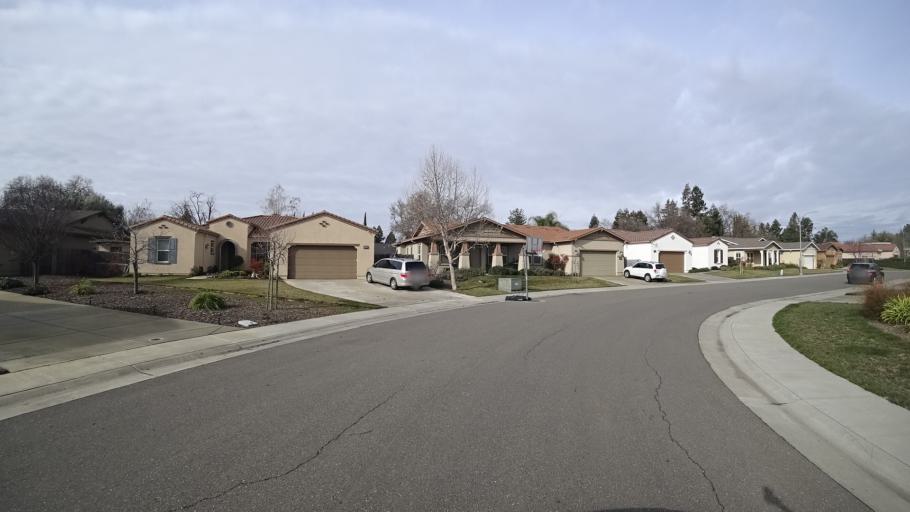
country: US
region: California
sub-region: Yolo County
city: Davis
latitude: 38.5398
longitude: -121.6979
